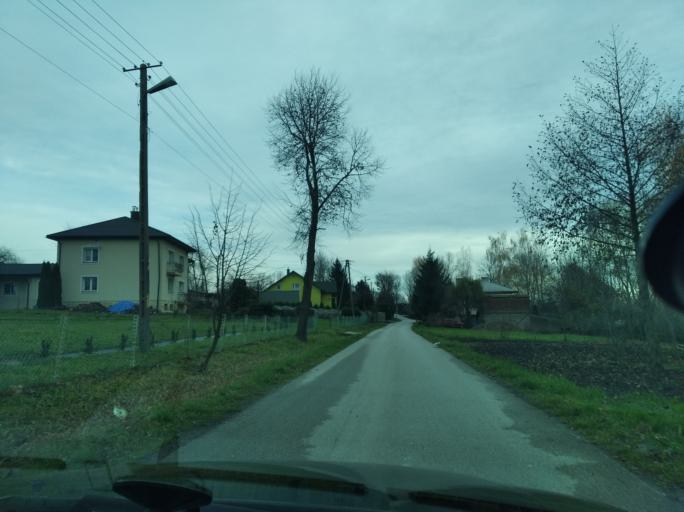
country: PL
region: Subcarpathian Voivodeship
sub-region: Powiat przeworski
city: Debow
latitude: 50.0487
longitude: 22.4346
